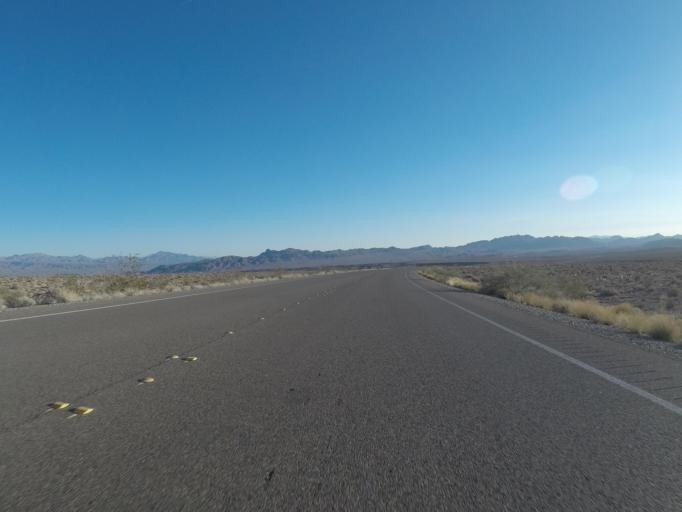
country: US
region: Nevada
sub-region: Clark County
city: Moapa Valley
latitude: 36.3560
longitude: -114.4828
